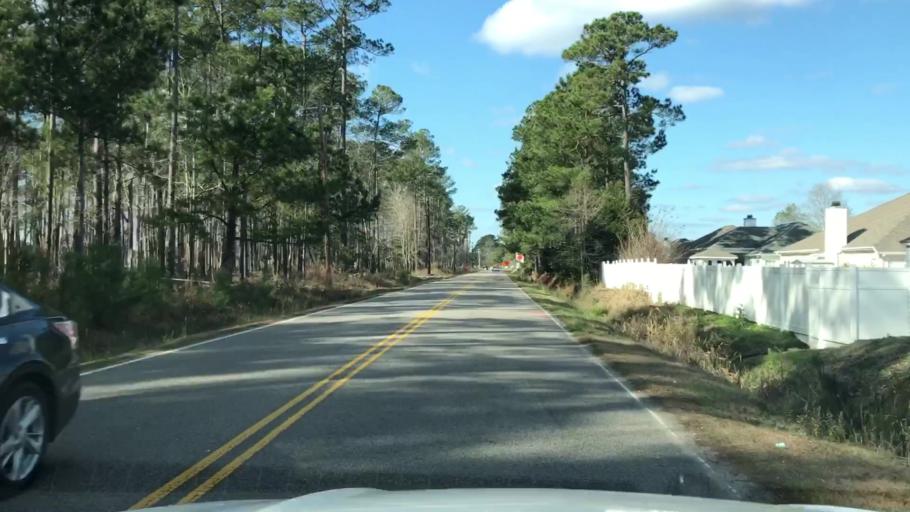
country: US
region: South Carolina
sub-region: Horry County
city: Socastee
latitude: 33.6582
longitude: -79.0013
